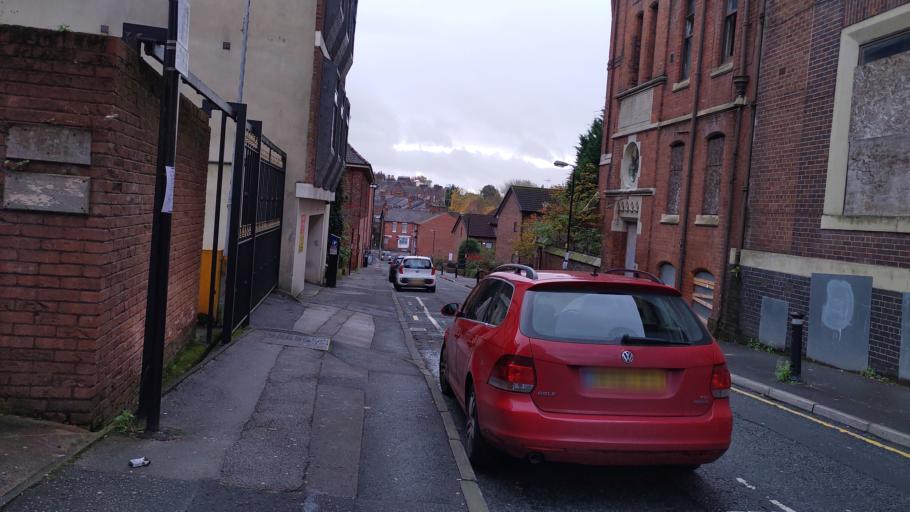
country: GB
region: England
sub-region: Lancashire
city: Preston
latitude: 53.7569
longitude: -2.7036
